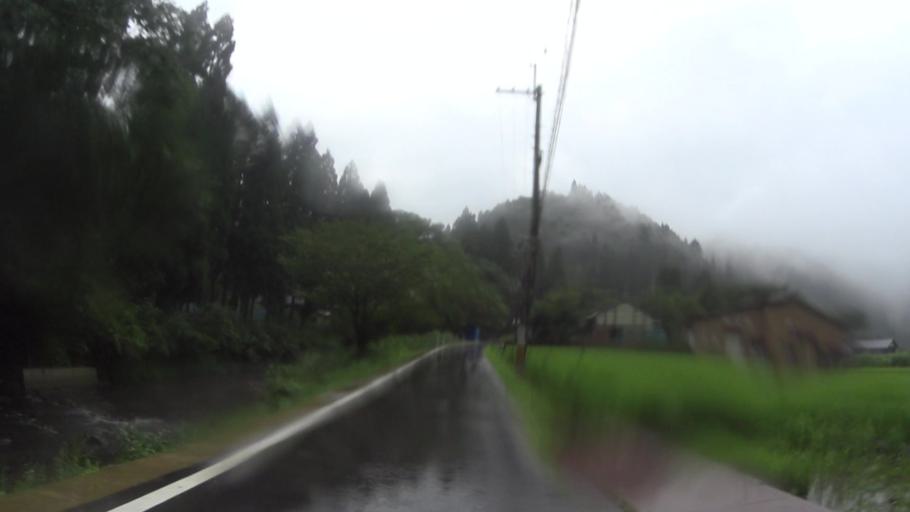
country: JP
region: Shiga Prefecture
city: Kitahama
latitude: 35.2649
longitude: 135.8213
